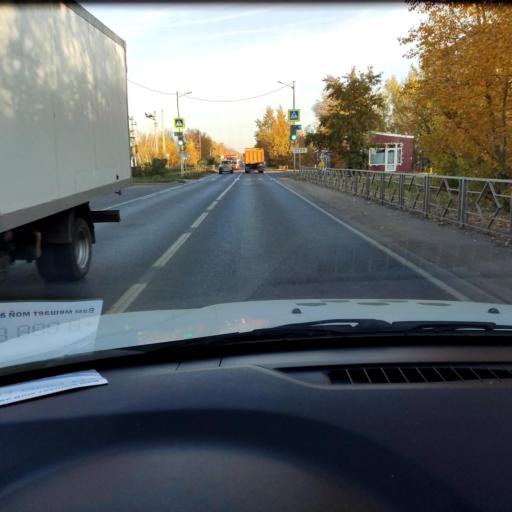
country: RU
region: Samara
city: Tol'yatti
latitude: 53.5395
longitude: 49.3932
